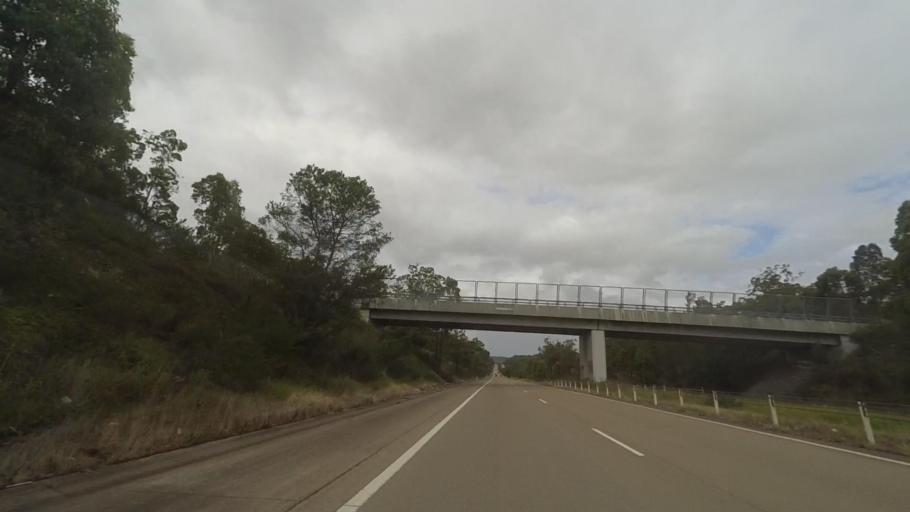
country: AU
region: New South Wales
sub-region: Port Stephens Shire
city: Medowie
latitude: -32.6407
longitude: 151.9303
